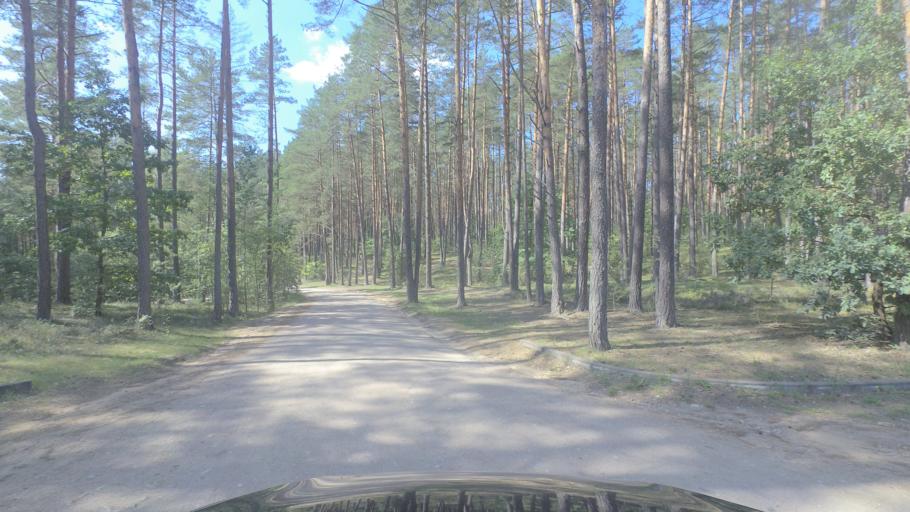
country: LT
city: Nemencine
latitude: 54.8487
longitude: 25.5017
